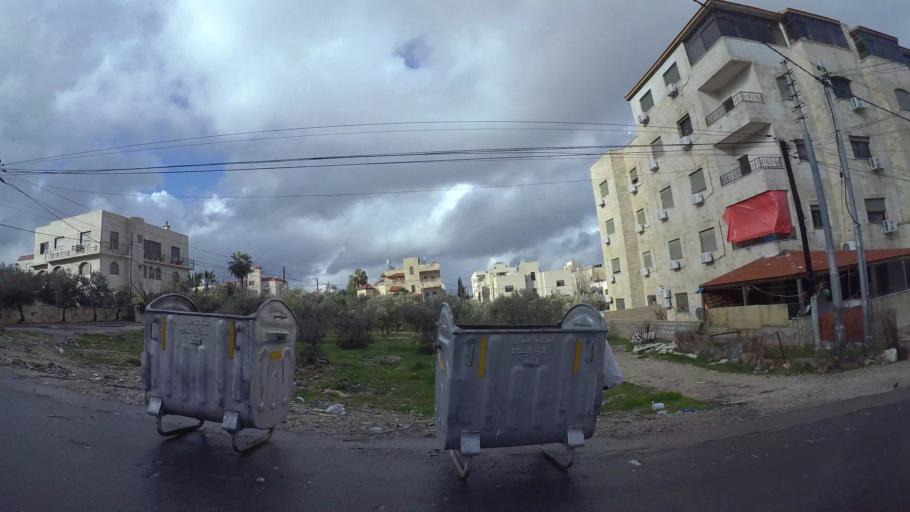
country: JO
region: Amman
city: Al Jubayhah
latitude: 32.0293
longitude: 35.8681
